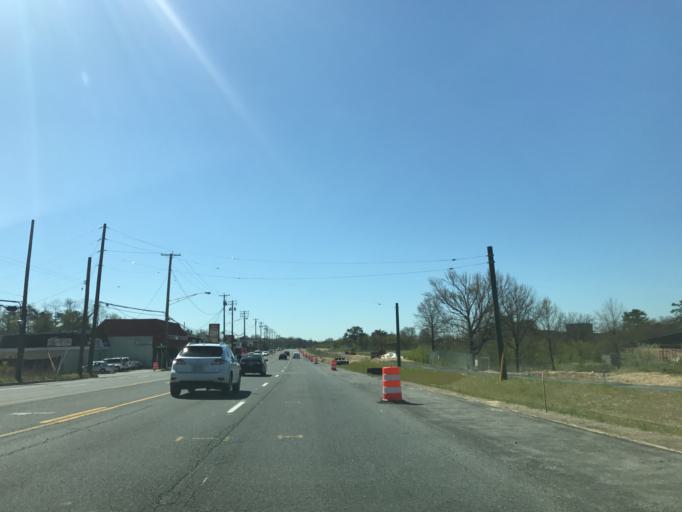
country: US
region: Maryland
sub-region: Anne Arundel County
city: Fort Meade
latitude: 39.1103
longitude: -76.7246
